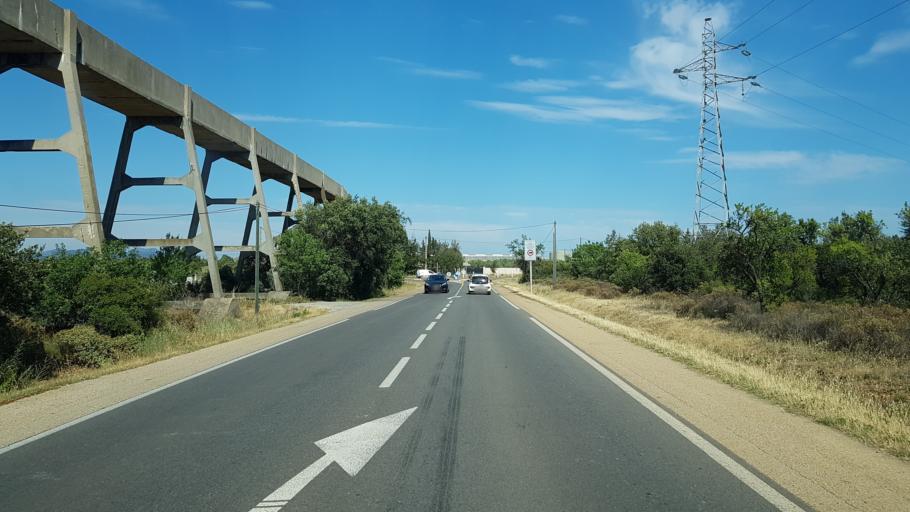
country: FR
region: Provence-Alpes-Cote d'Azur
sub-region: Departement des Bouches-du-Rhone
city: Saint-Martin-de-Crau
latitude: 43.6657
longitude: 4.7965
